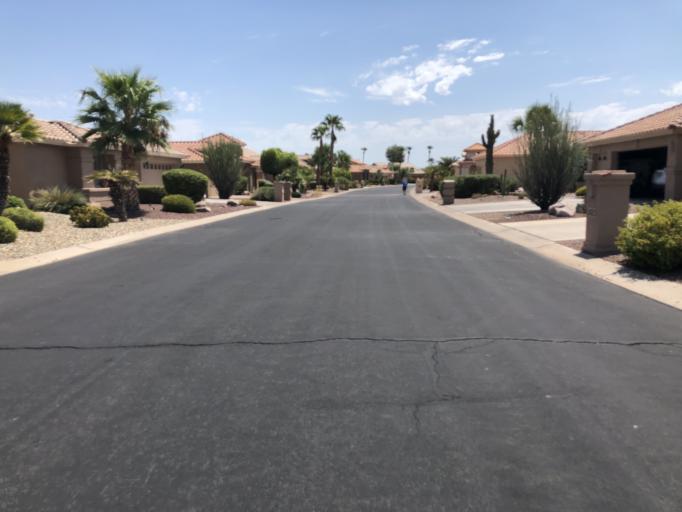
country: US
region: Arizona
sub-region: Maricopa County
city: Sun Lakes
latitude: 33.2285
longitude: -111.8844
